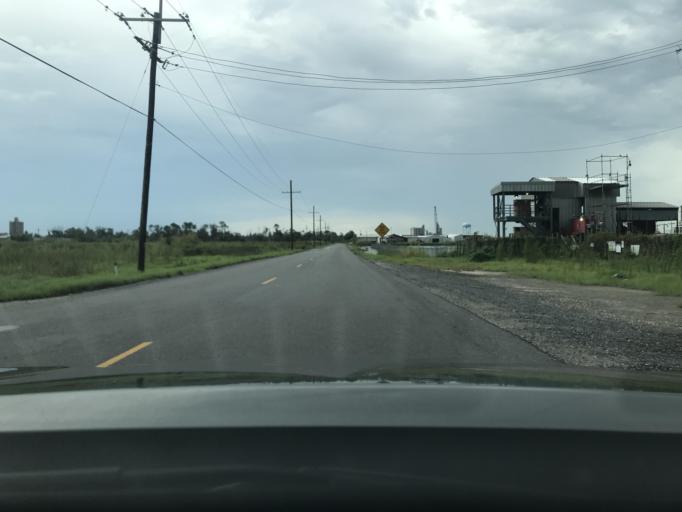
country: US
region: Louisiana
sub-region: Calcasieu Parish
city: Westlake
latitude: 30.2309
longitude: -93.2523
